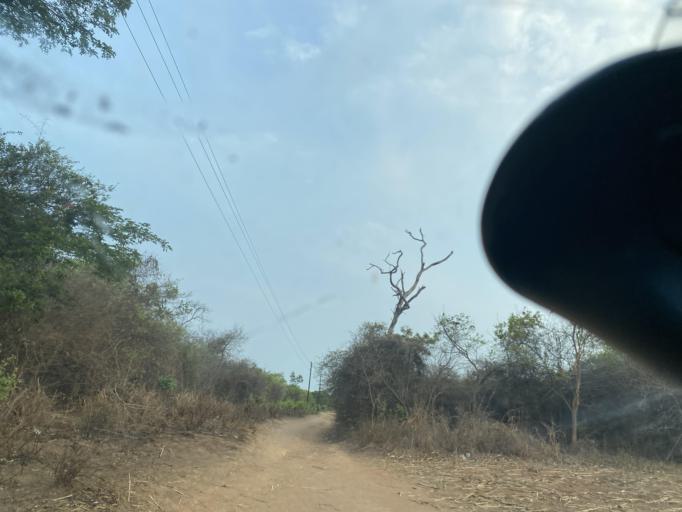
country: ZM
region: Lusaka
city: Chongwe
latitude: -15.2044
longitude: 28.4980
